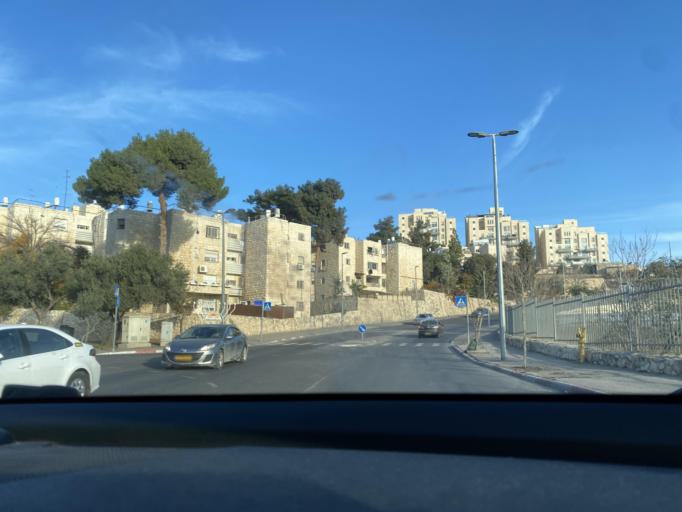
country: PS
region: West Bank
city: Ash Shaykh Sa`d
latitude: 31.7447
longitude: 35.2394
